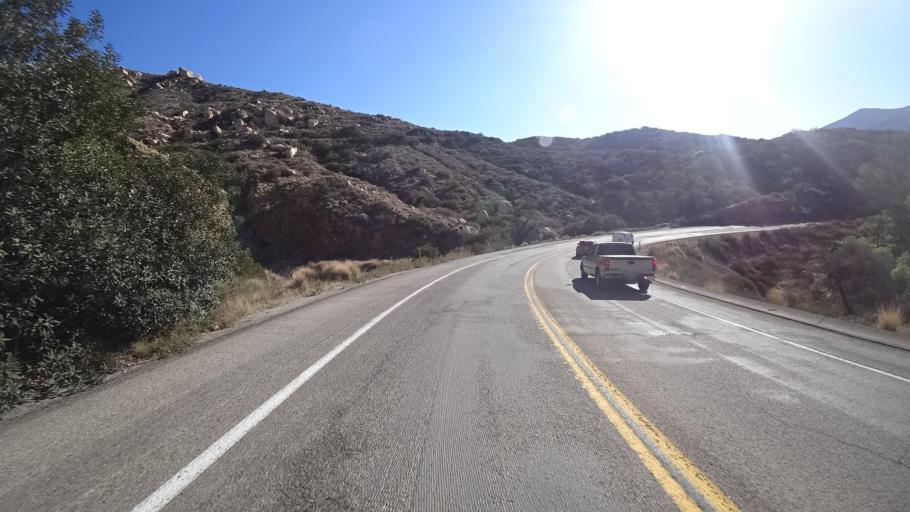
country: MX
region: Baja California
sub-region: Tecate
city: Lomas de Santa Anita
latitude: 32.6191
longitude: -116.7282
